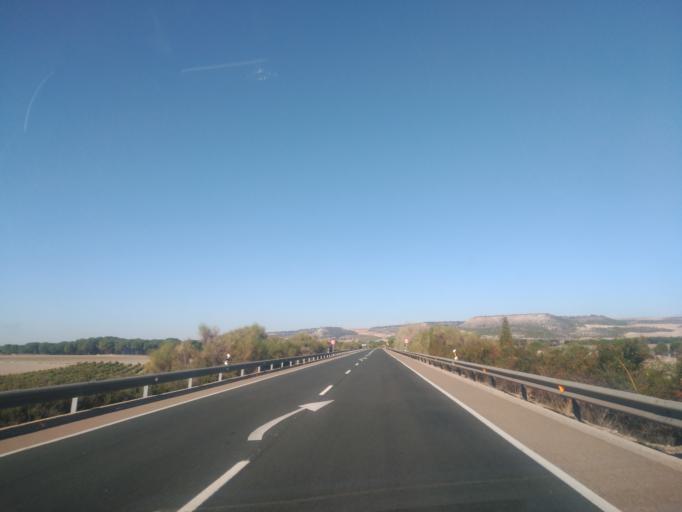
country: ES
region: Castille and Leon
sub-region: Provincia de Valladolid
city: Quintanilla de Onesimo
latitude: 41.6204
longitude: -4.3729
